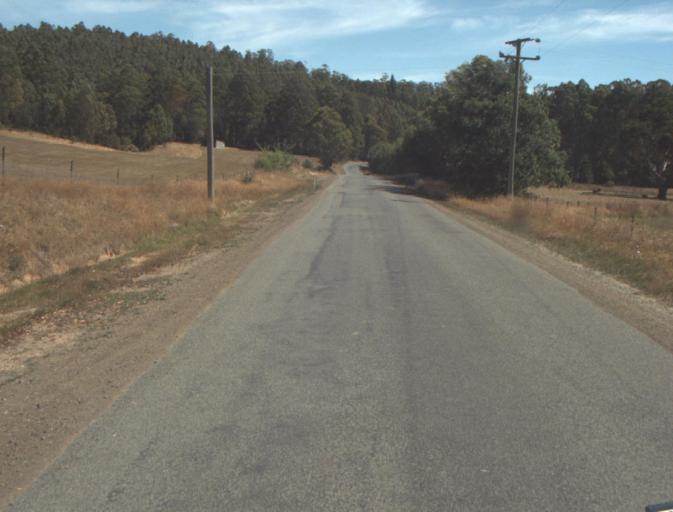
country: AU
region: Tasmania
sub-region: Dorset
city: Scottsdale
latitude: -41.3106
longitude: 147.3917
